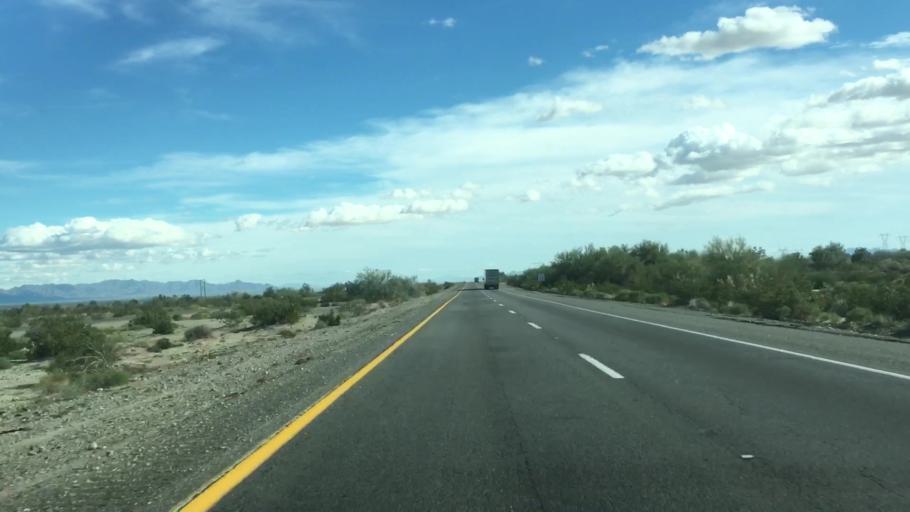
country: US
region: California
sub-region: Riverside County
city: Mesa Verde
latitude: 33.6789
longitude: -115.2324
